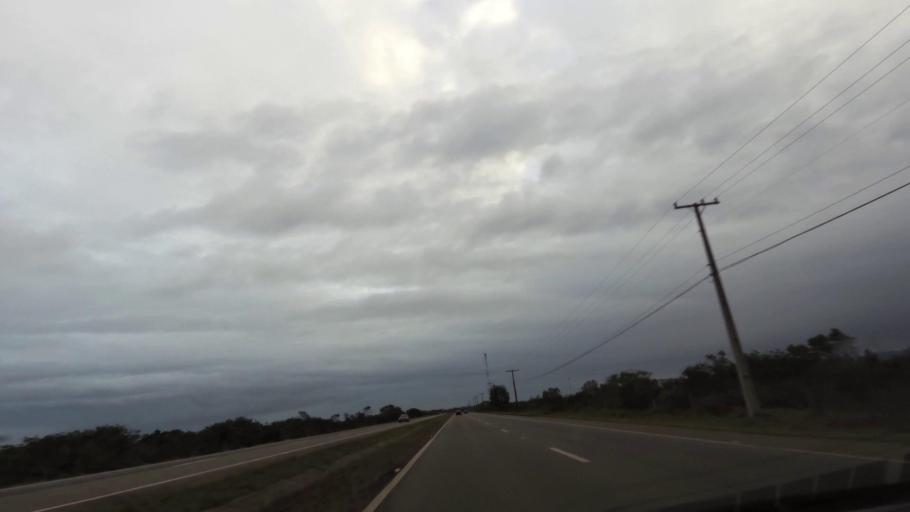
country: BR
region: Espirito Santo
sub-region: Guarapari
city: Guarapari
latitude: -20.5740
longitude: -40.4137
